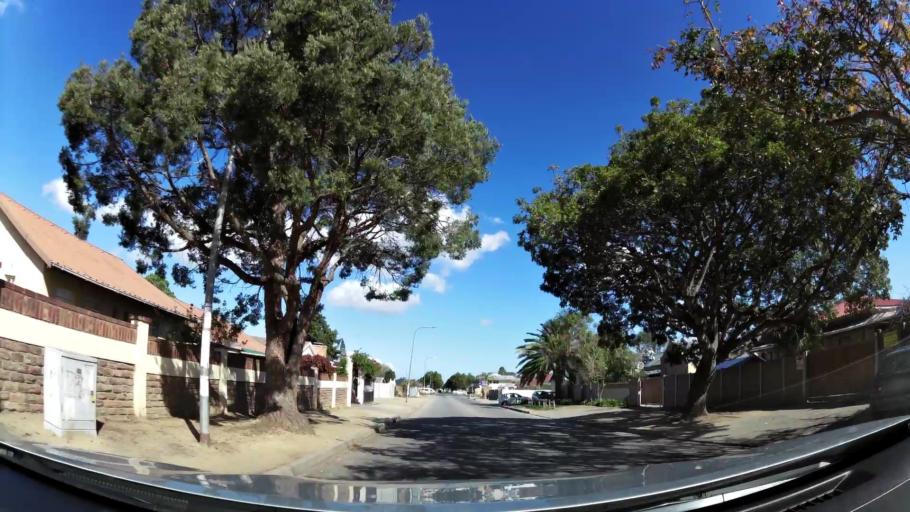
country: ZA
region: Western Cape
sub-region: Eden District Municipality
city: George
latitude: -33.9653
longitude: 22.4589
